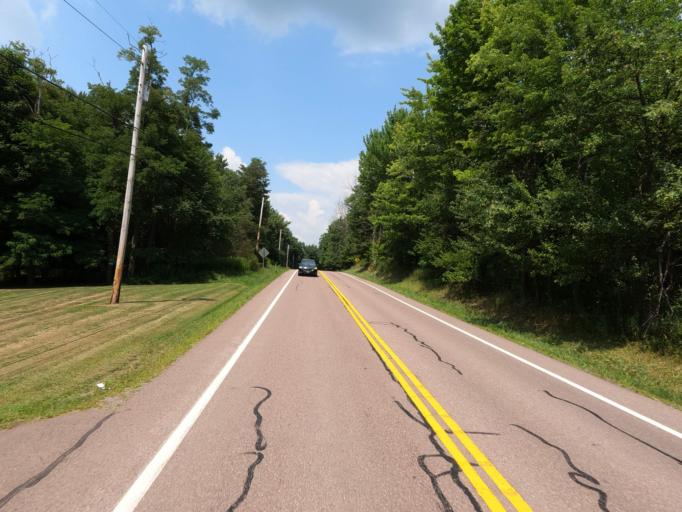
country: US
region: Maryland
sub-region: Allegany County
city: Westernport
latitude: 39.6457
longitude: -79.1986
